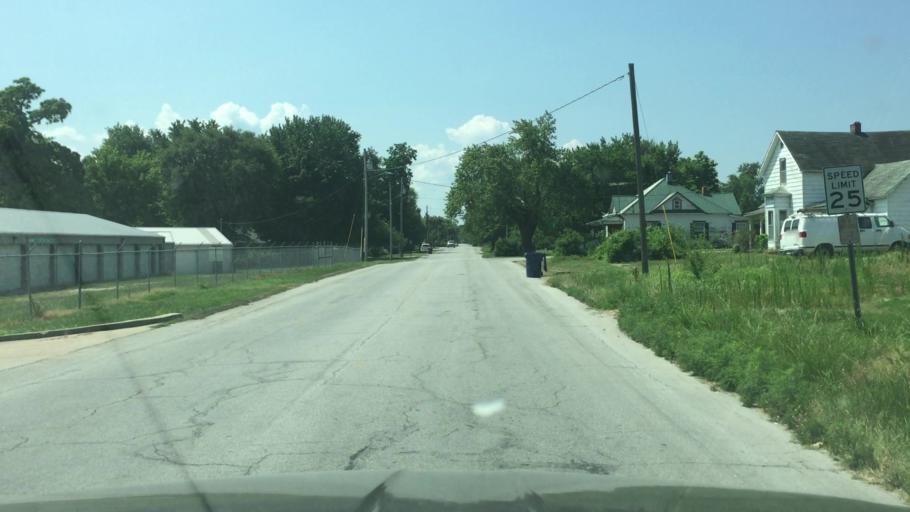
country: US
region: Missouri
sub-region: Miller County
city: Eldon
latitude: 38.3461
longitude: -92.5864
